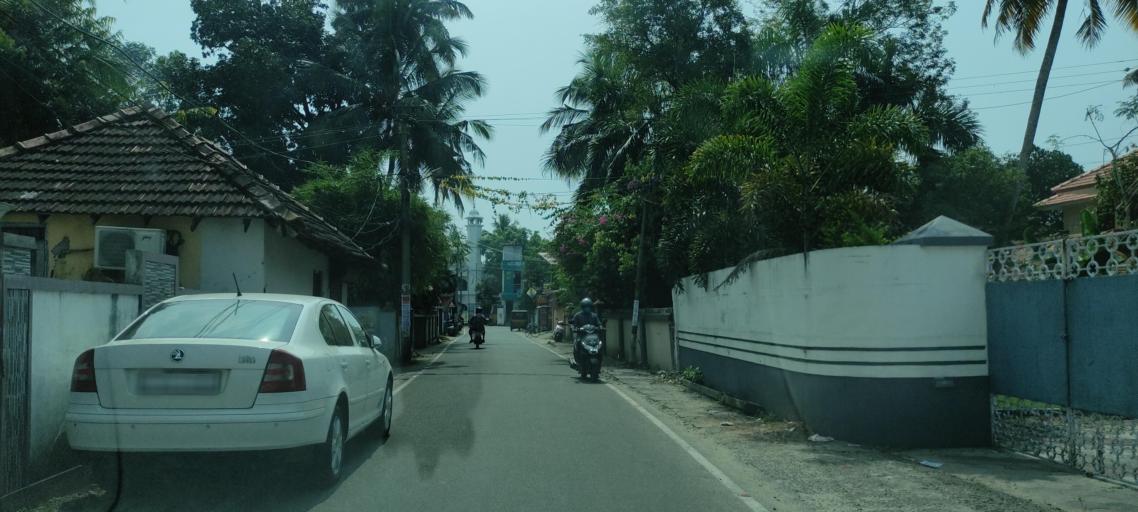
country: IN
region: Kerala
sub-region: Alappuzha
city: Alleppey
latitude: 9.5037
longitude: 76.3334
